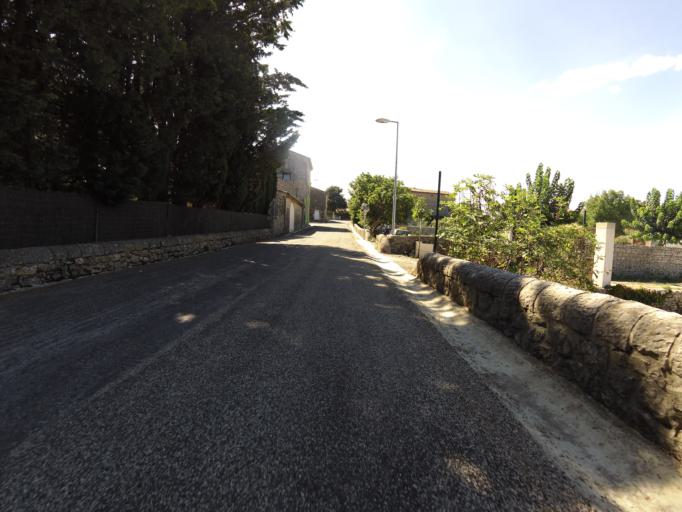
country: FR
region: Languedoc-Roussillon
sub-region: Departement du Gard
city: Quissac
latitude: 43.9557
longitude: 4.0309
